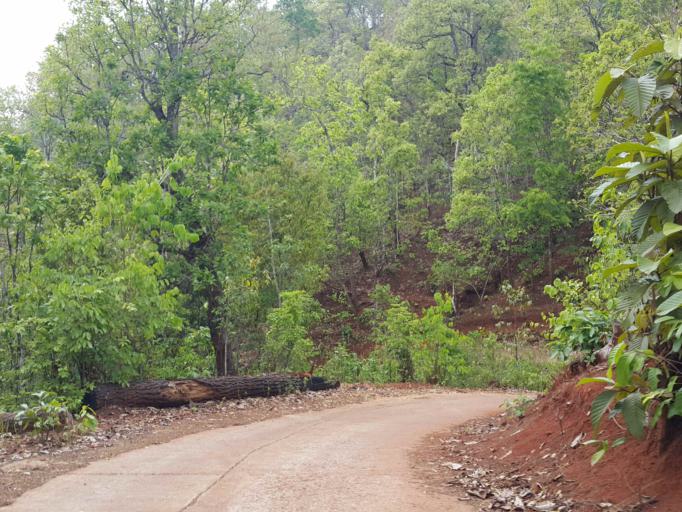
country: TH
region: Chiang Mai
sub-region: Amphoe Chiang Dao
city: Chiang Dao
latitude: 19.3049
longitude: 98.7286
